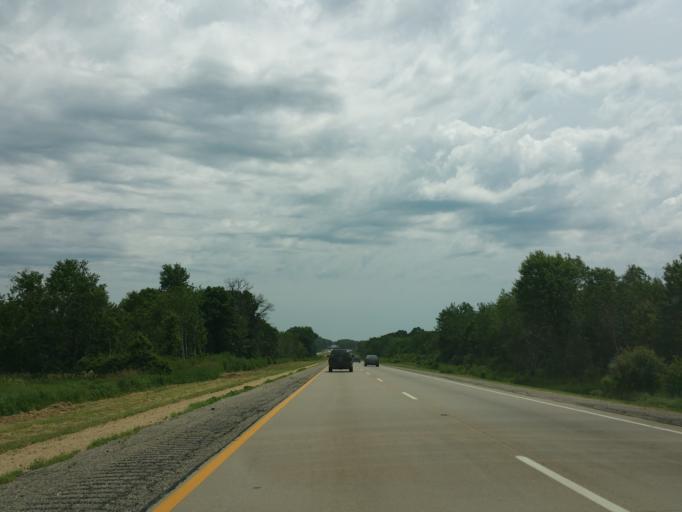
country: US
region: Wisconsin
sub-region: Columbia County
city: Wisconsin Dells
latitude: 43.6878
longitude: -89.8458
